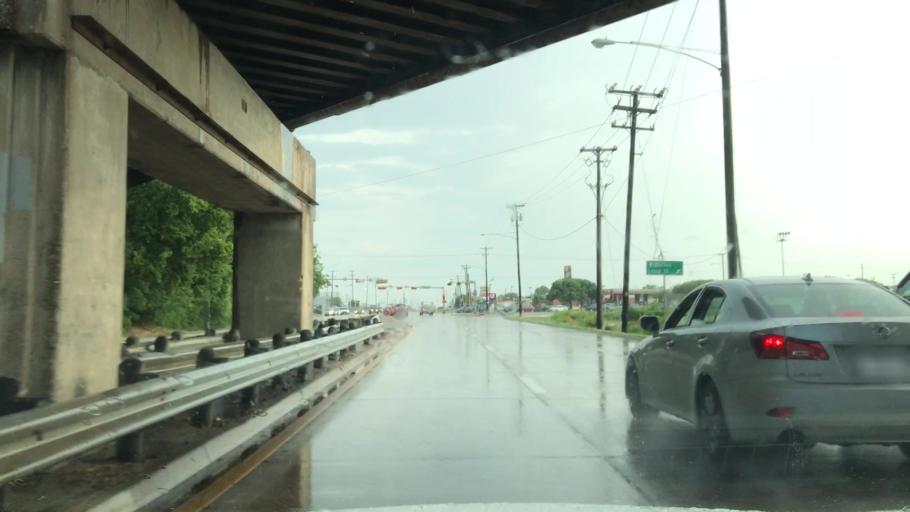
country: US
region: Texas
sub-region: Dallas County
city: Garland
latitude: 32.8655
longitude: -96.6699
